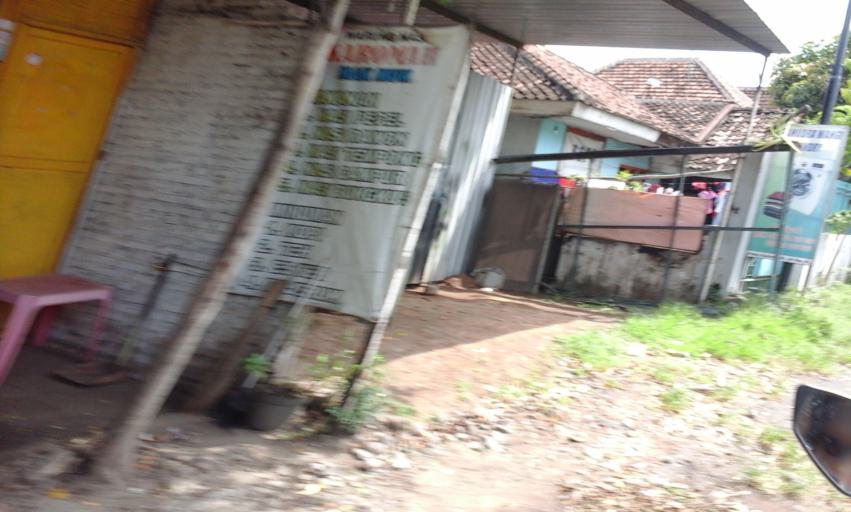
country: ID
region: East Java
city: Kepuh Wetan
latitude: -8.2495
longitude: 114.3466
